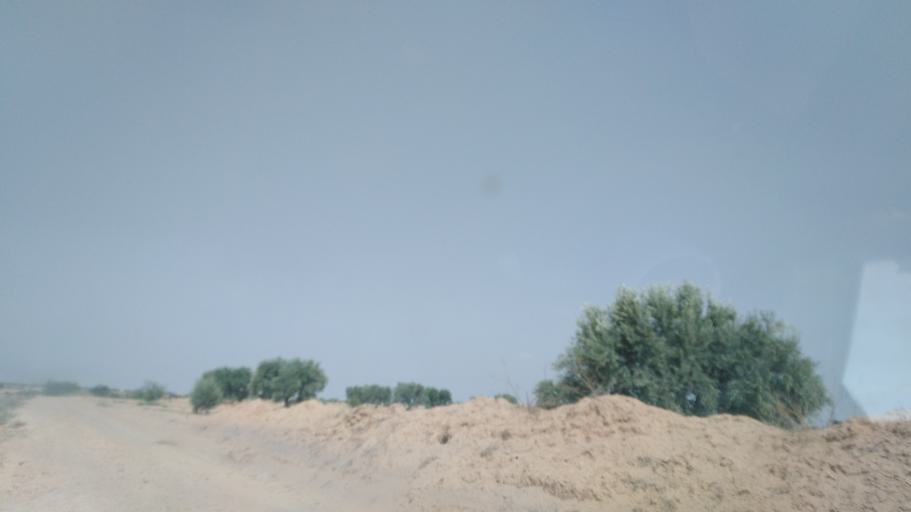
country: TN
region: Safaqis
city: Sfax
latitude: 34.6470
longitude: 10.5586
